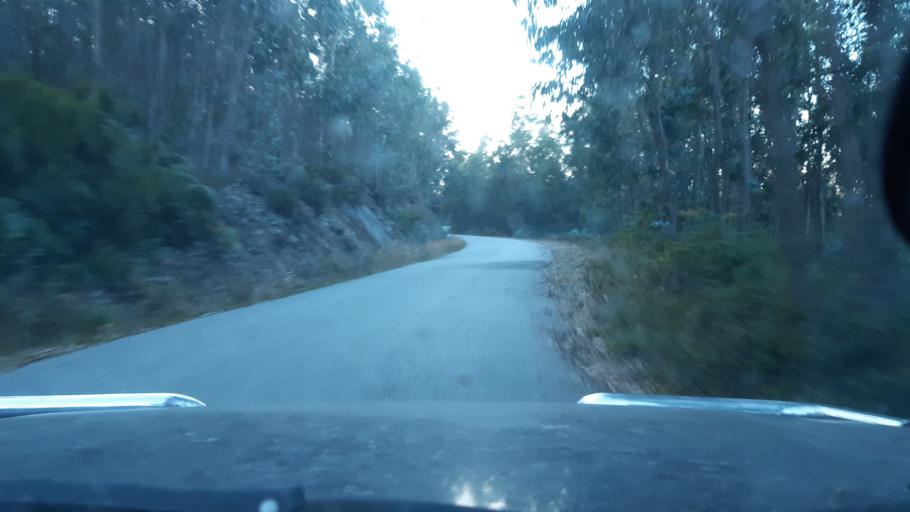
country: PT
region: Aveiro
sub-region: Agueda
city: Aguada de Cima
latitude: 40.5515
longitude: -8.2839
